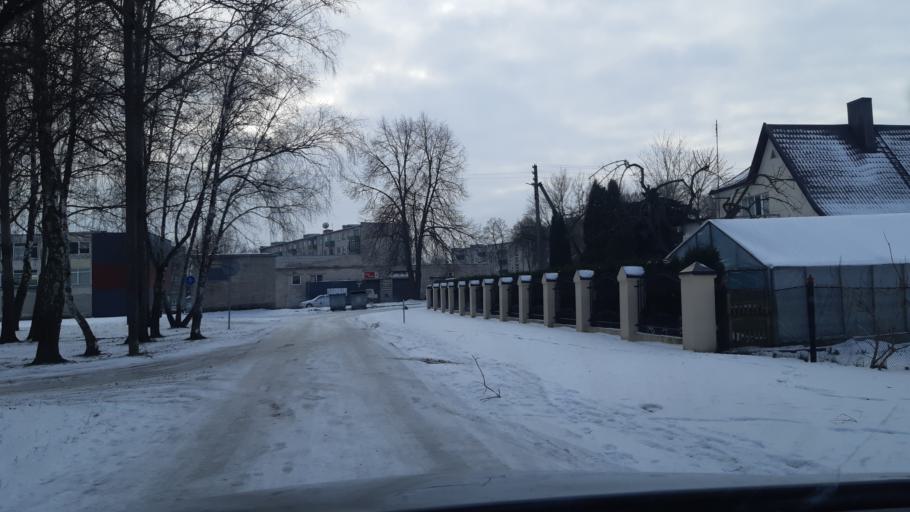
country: LT
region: Kauno apskritis
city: Kedainiai
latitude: 55.2920
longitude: 23.9835
